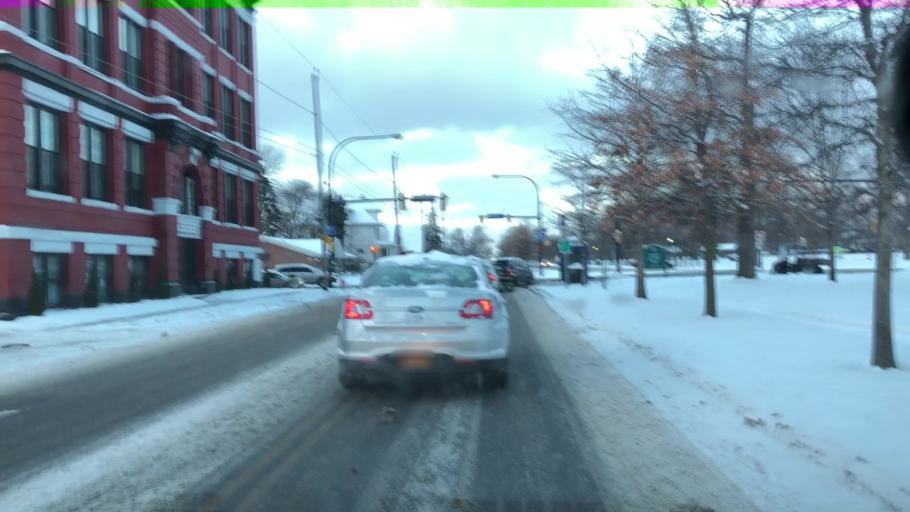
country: US
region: New York
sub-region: Erie County
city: Buffalo
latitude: 42.9037
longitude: -78.8386
